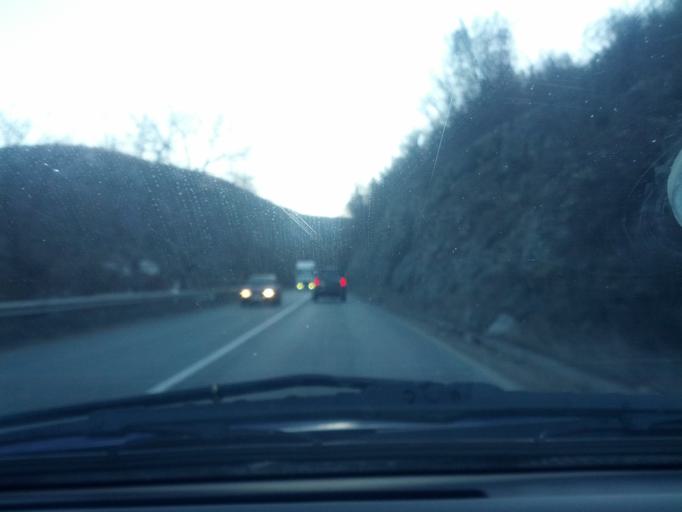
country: BG
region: Vratsa
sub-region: Obshtina Mezdra
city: Mezdra
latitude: 43.0537
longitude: 23.6828
